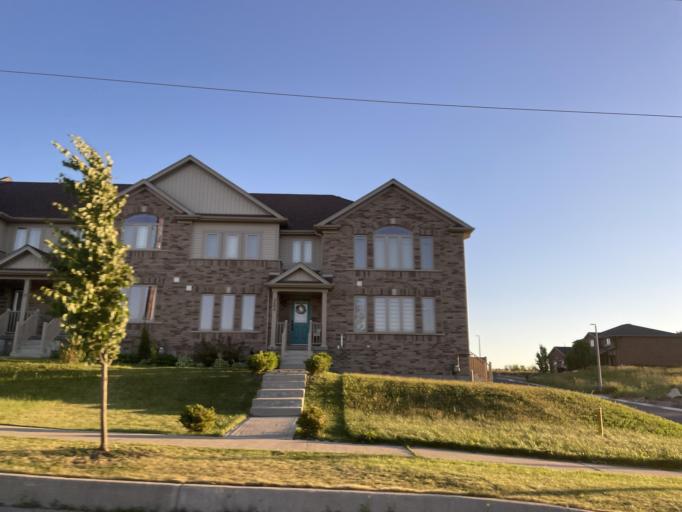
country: CA
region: Ontario
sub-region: Wellington County
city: Guelph
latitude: 43.5839
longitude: -80.2685
